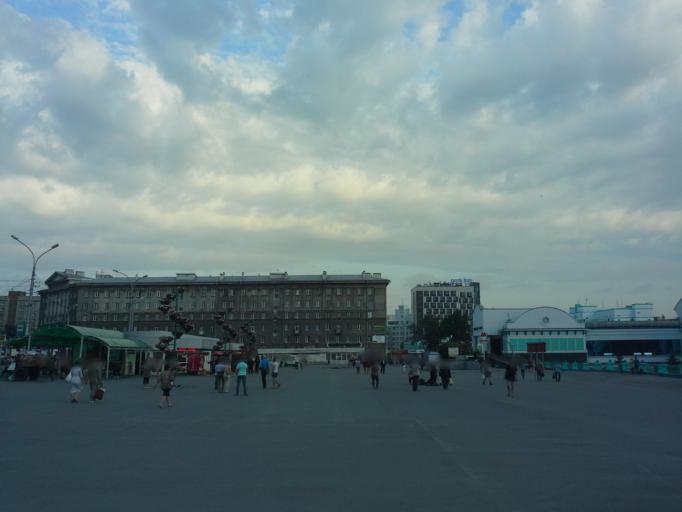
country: RU
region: Novosibirsk
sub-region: Novosibirskiy Rayon
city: Novosibirsk
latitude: 55.0358
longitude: 82.8976
